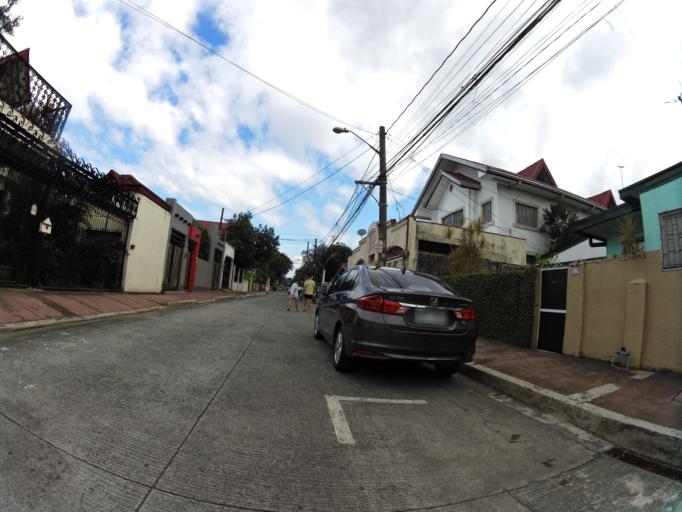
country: PH
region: Calabarzon
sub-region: Province of Rizal
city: Antipolo
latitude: 14.6396
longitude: 121.1137
